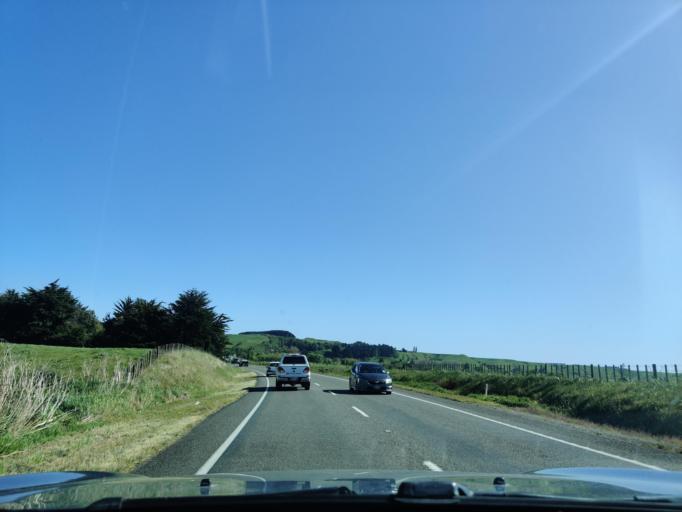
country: NZ
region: Manawatu-Wanganui
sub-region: Wanganui District
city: Wanganui
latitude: -40.0128
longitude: 175.1728
